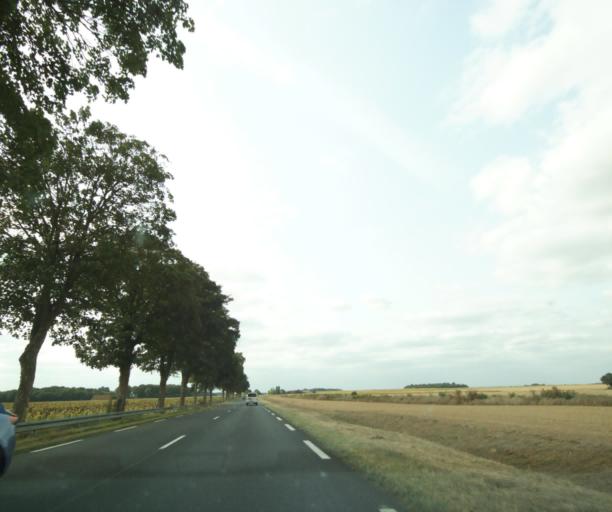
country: FR
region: Centre
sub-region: Departement d'Indre-et-Loire
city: Truyes
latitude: 47.2387
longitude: 0.8654
